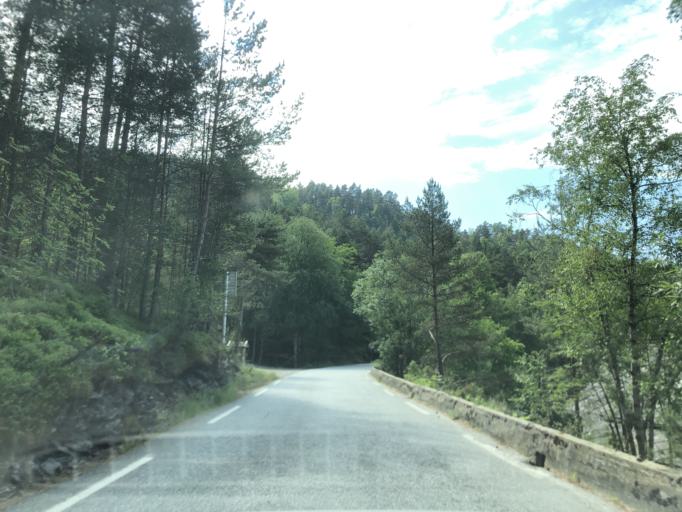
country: NO
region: Hordaland
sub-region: Jondal
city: Jondal
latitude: 60.3389
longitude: 6.3673
